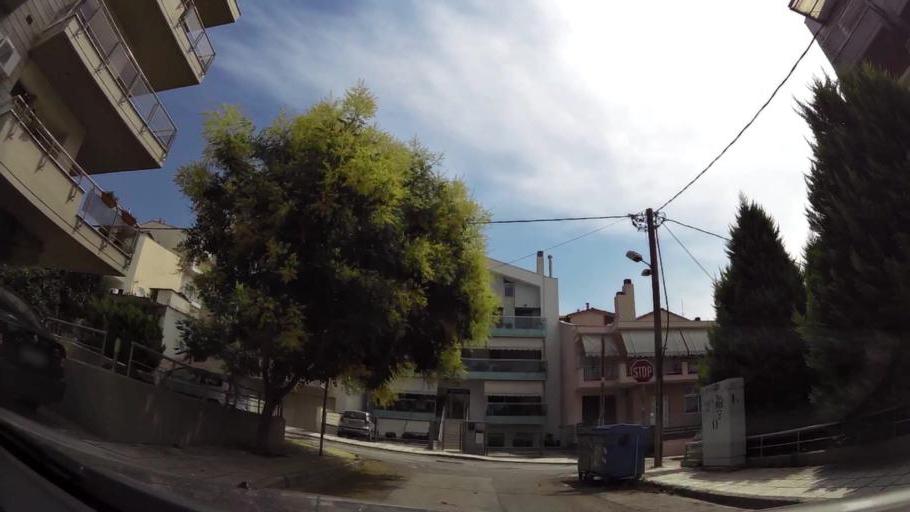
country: GR
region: Central Macedonia
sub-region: Nomos Thessalonikis
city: Pylaia
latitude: 40.5960
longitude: 22.9888
